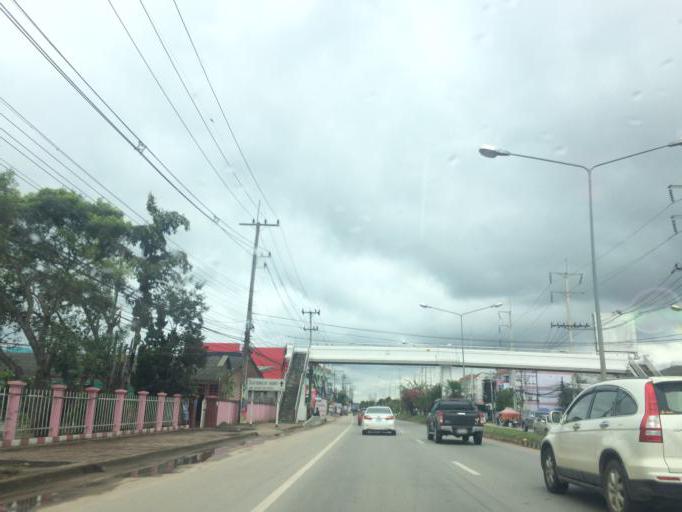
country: TH
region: Chiang Rai
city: Mae Chan
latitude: 20.0470
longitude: 99.8761
